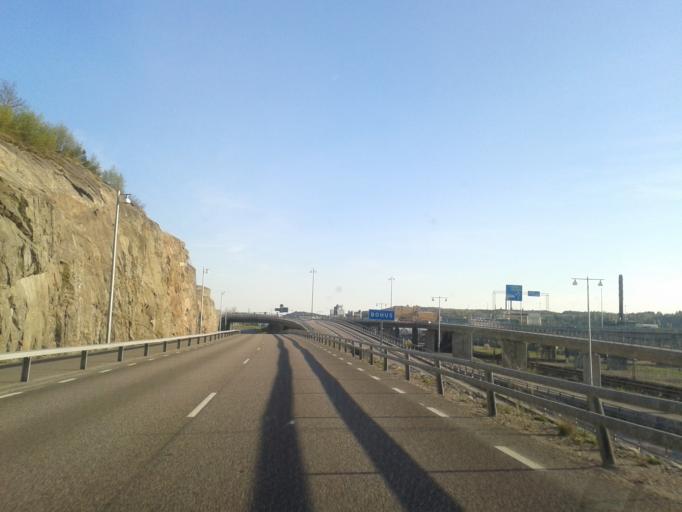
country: SE
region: Vaestra Goetaland
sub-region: Ale Kommun
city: Surte
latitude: 57.8561
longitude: 12.0162
